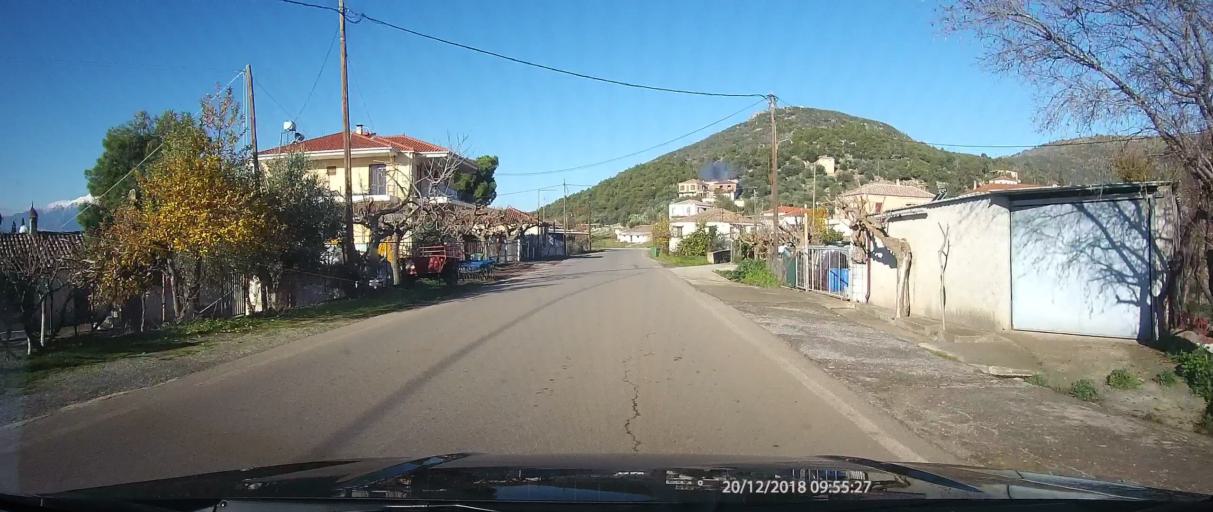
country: GR
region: Peloponnese
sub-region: Nomos Lakonias
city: Yerakion
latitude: 37.0245
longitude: 22.6227
